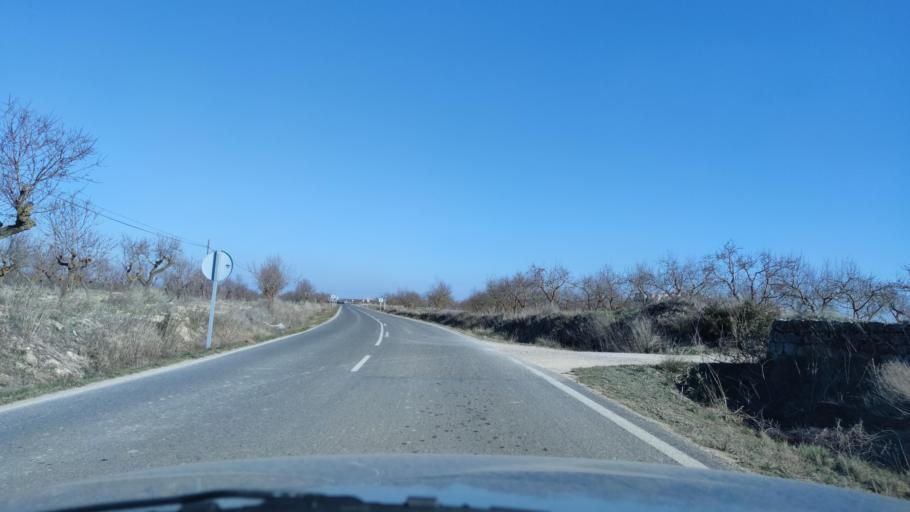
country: ES
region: Catalonia
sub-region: Provincia de Lleida
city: Maials
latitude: 41.3636
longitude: 0.4912
